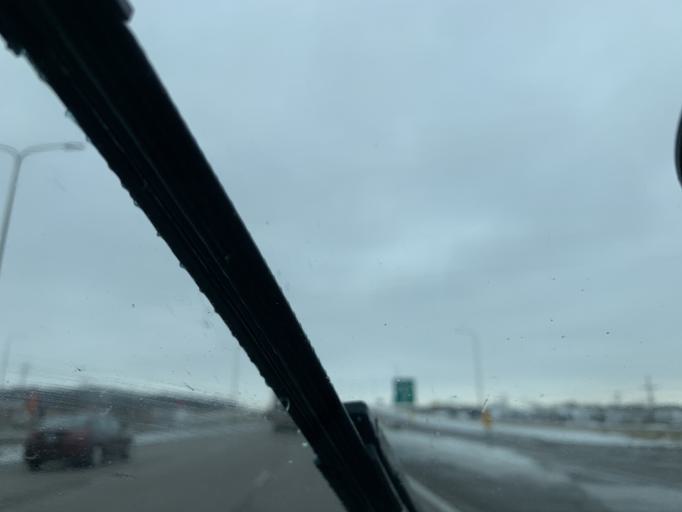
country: US
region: Minnesota
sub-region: Washington County
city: Newport
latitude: 44.8751
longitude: -93.0017
